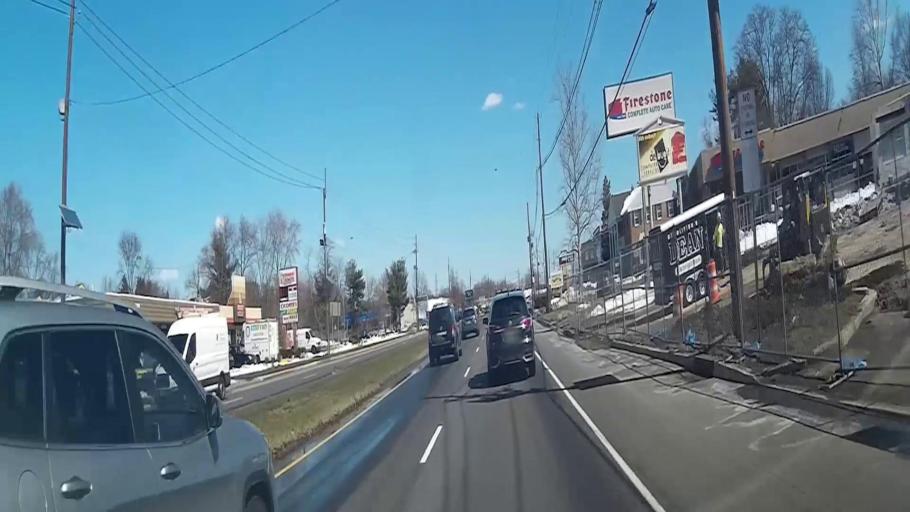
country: US
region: New Jersey
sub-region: Camden County
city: Greentree
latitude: 39.8957
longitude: -74.9434
